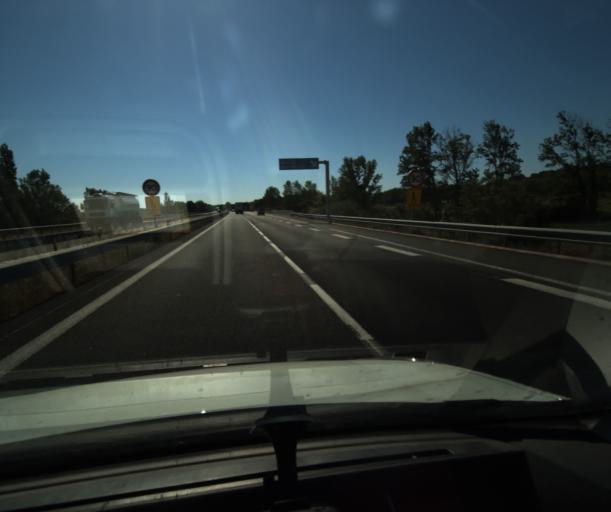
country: FR
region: Languedoc-Roussillon
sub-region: Departement de l'Aude
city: Fabrezan
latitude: 43.1714
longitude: 2.6981
